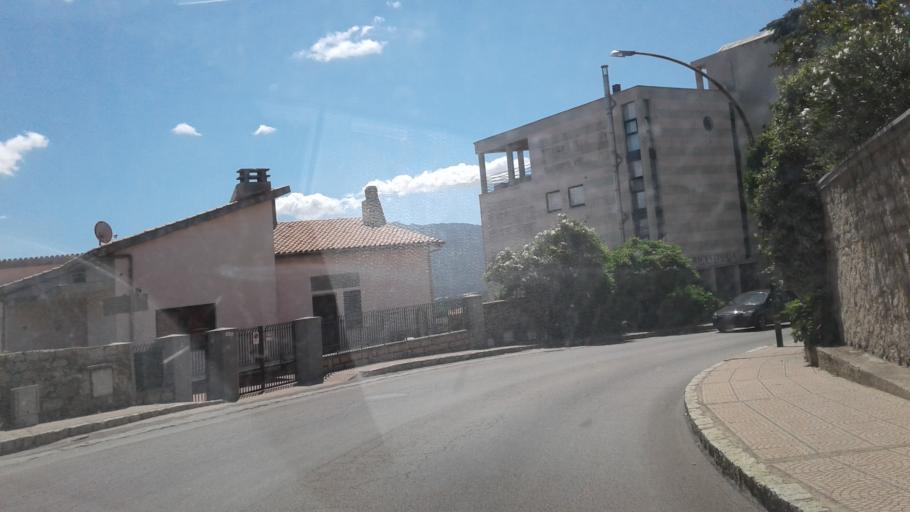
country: IT
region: Sardinia
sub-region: Provincia di Olbia-Tempio
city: Tempio Pausania
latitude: 40.9045
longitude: 9.1072
